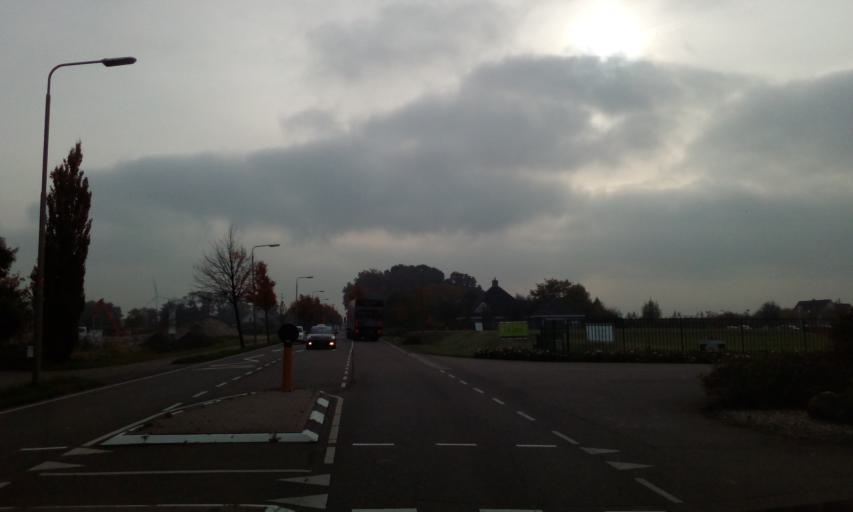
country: NL
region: South Holland
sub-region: Gemeente Waddinxveen
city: Groenswaard
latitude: 52.0266
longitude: 4.6049
